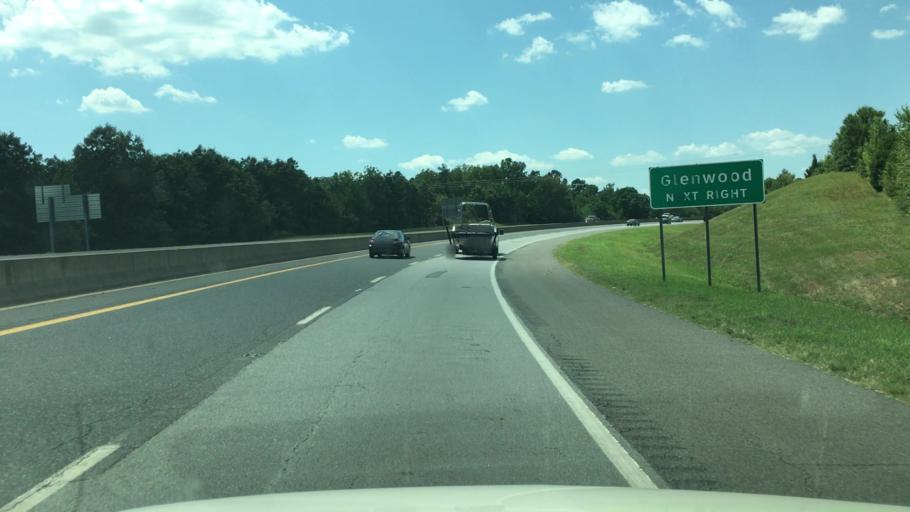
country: US
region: Arkansas
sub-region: Garland County
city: Rockwell
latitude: 34.4708
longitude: -93.1107
